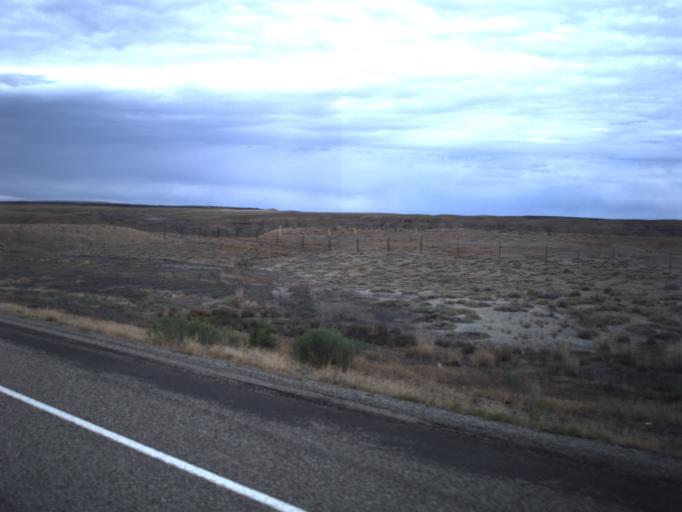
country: US
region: Colorado
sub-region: Mesa County
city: Loma
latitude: 39.1184
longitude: -109.1762
